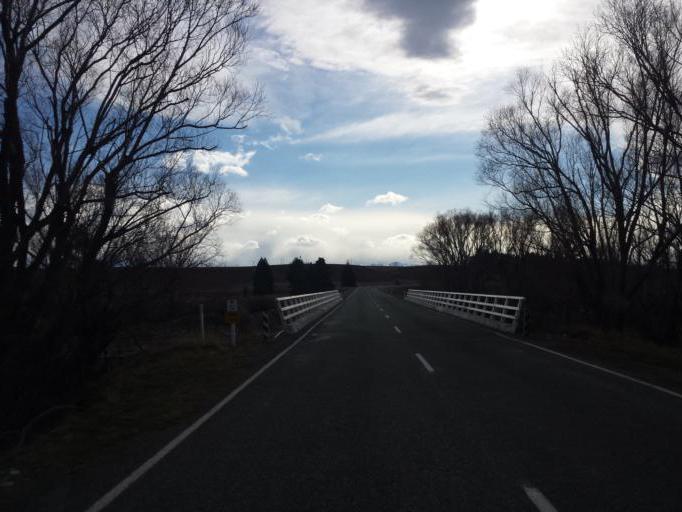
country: NZ
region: Canterbury
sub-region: Timaru District
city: Pleasant Point
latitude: -44.0596
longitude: 170.5028
